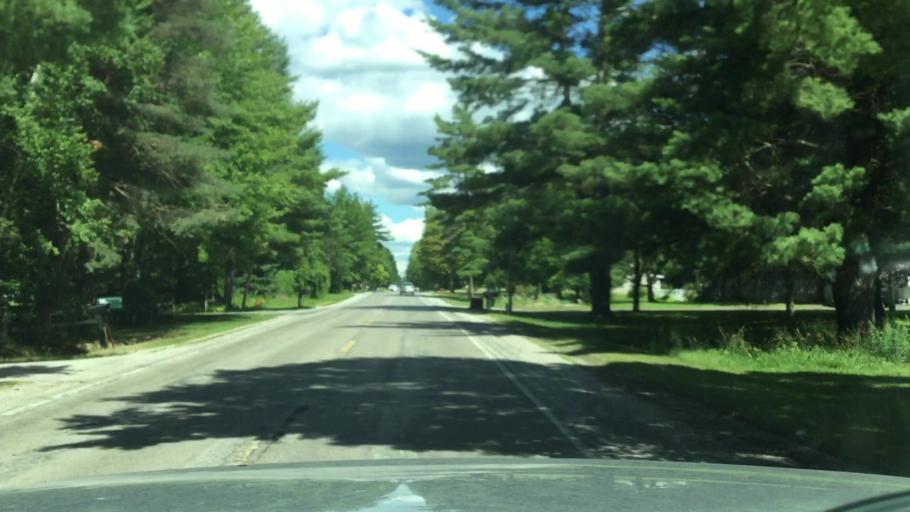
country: US
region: Michigan
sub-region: Saginaw County
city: Saint Charles
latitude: 43.3797
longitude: -84.1401
